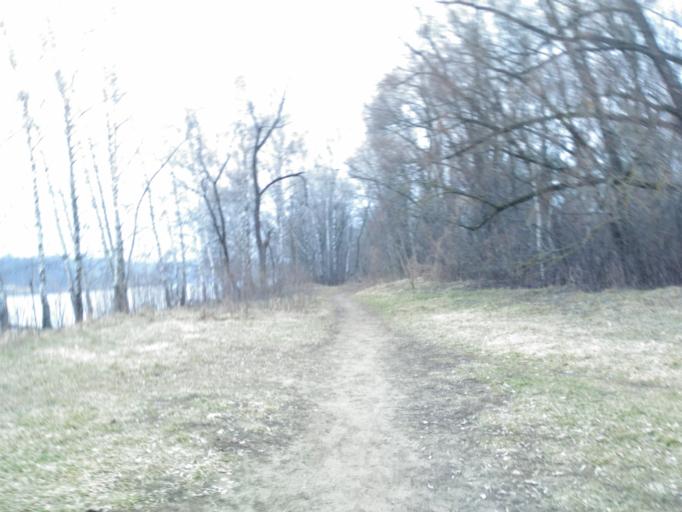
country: RU
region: Moscow
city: Shchukino
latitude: 55.7757
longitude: 37.4230
